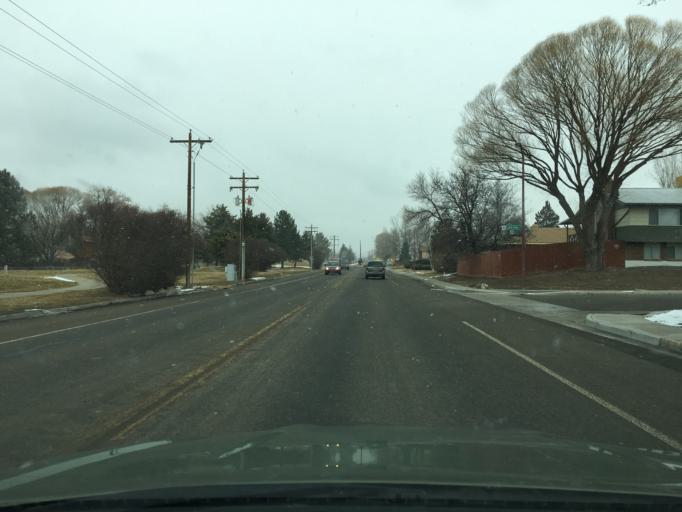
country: US
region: Colorado
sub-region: Montrose County
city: Montrose
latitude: 38.4725
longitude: -107.8566
